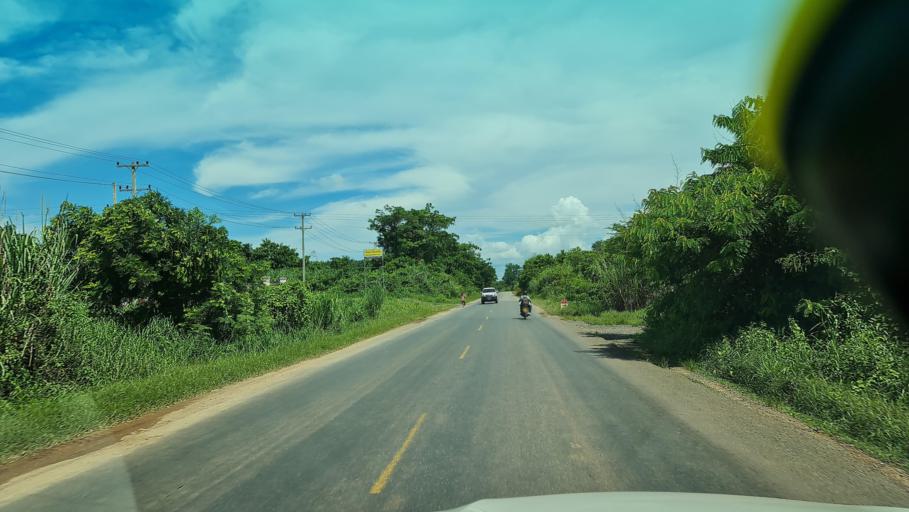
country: LA
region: Bolikhamxai
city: Ban Nahin
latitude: 18.2887
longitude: 104.1367
